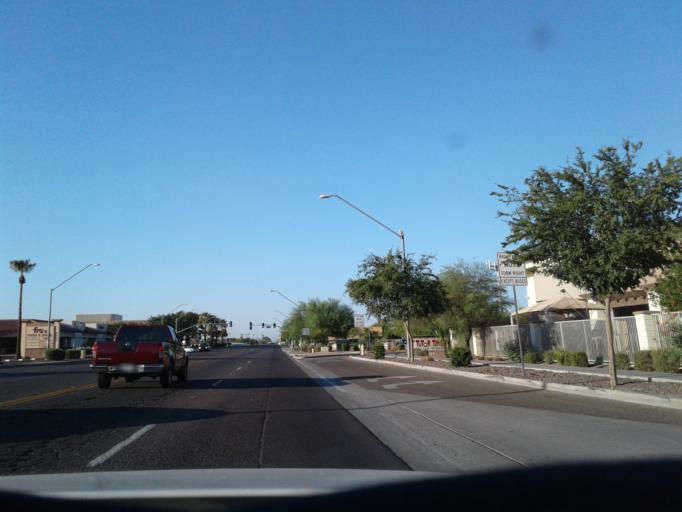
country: US
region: Arizona
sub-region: Maricopa County
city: Peoria
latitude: 33.6121
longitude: -112.1859
